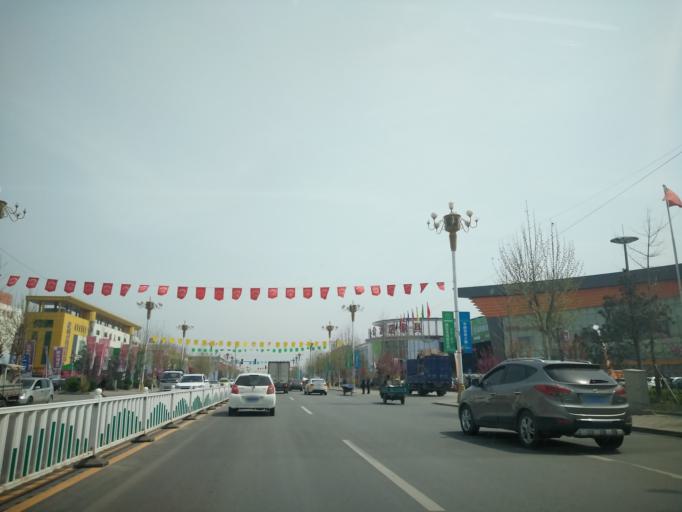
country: CN
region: Tianjin Shi
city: Xiawuqi
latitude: 39.7492
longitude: 117.0139
